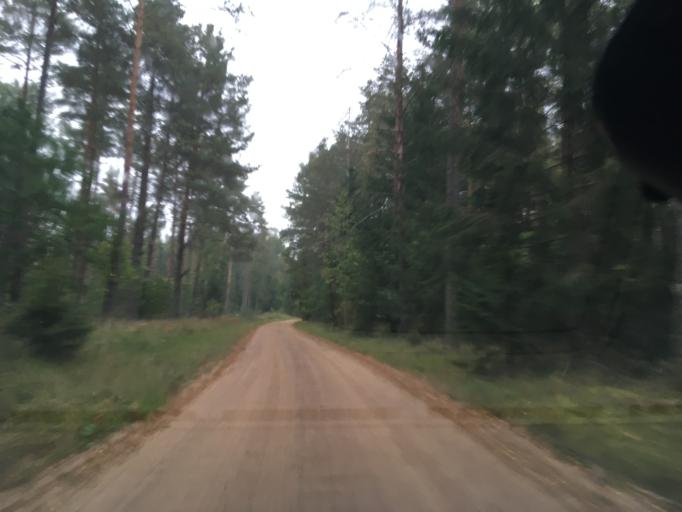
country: LV
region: Kuldigas Rajons
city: Kuldiga
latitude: 57.0151
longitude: 21.9881
